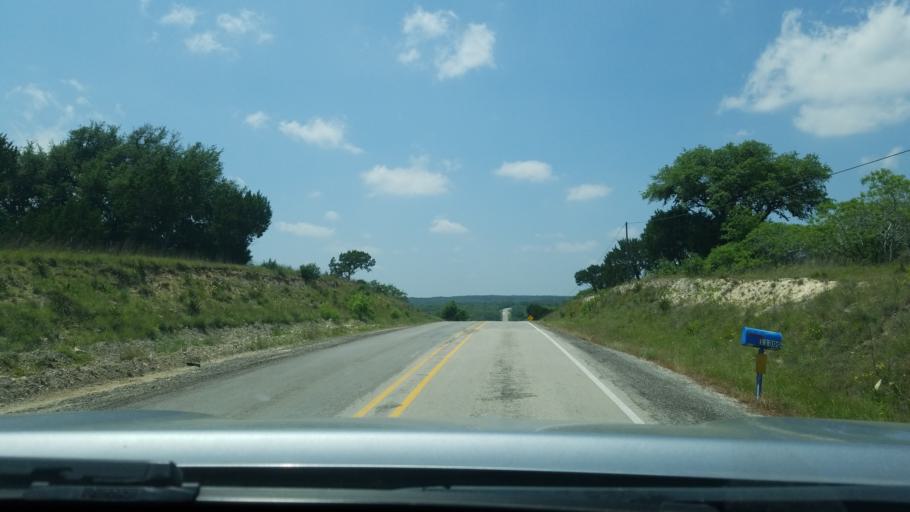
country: US
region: Texas
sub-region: Hays County
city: Woodcreek
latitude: 30.0984
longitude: -98.2447
